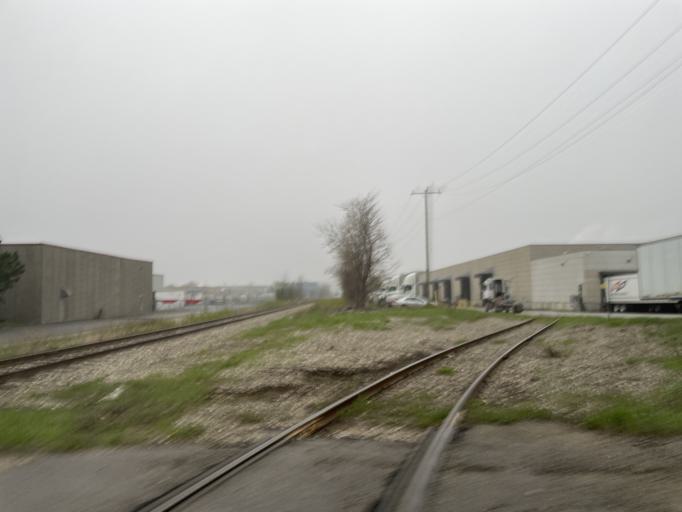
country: CA
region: Ontario
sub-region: Wellington County
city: Guelph
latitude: 43.5447
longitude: -80.3009
